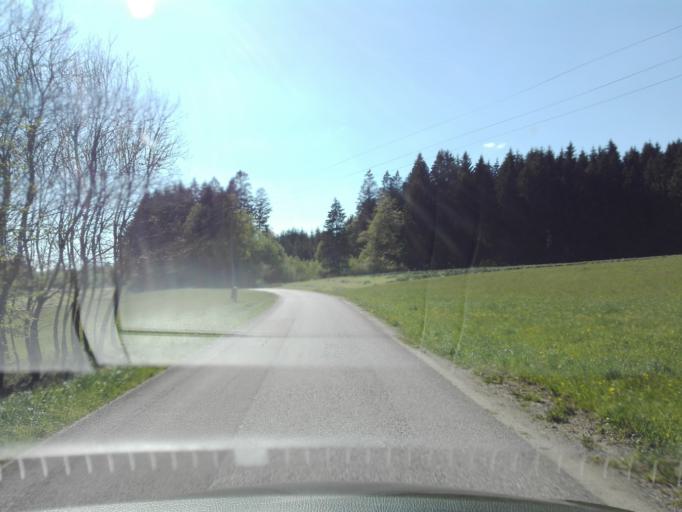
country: DE
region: Bavaria
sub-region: Lower Bavaria
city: Obernzell
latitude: 48.4473
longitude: 13.6962
